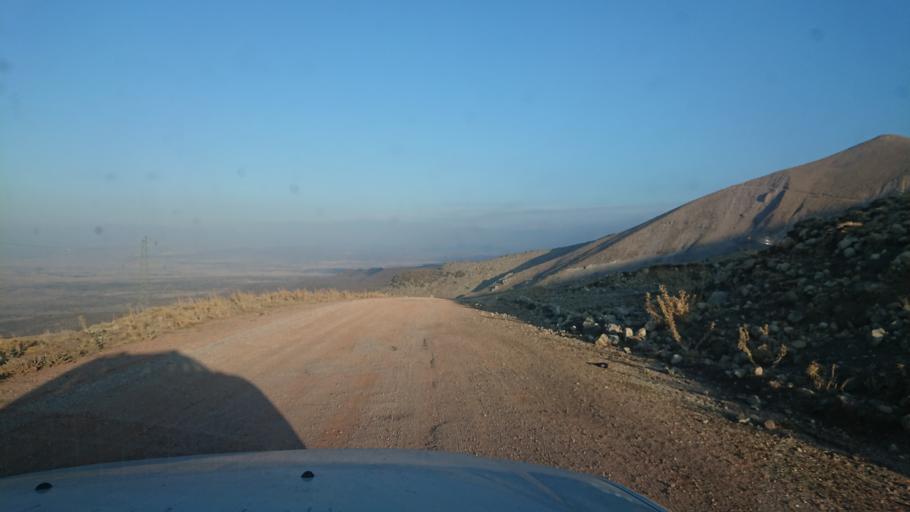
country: TR
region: Aksaray
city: Taspinar
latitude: 38.1593
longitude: 34.1678
